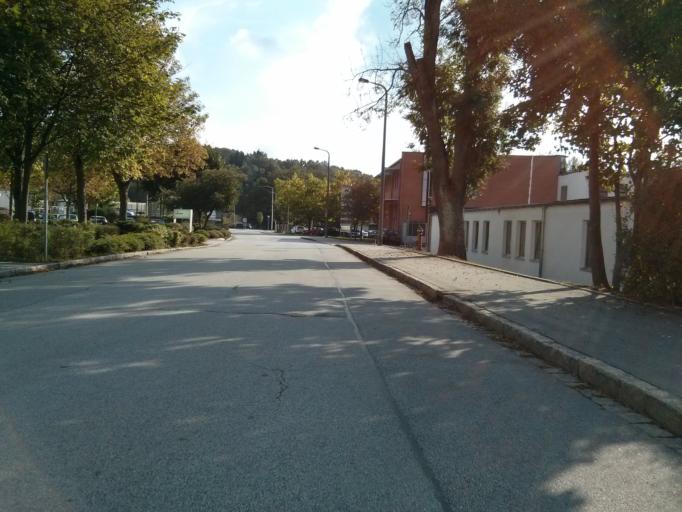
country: DE
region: Bavaria
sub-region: Lower Bavaria
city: Deggendorf
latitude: 48.8512
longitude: 12.9840
